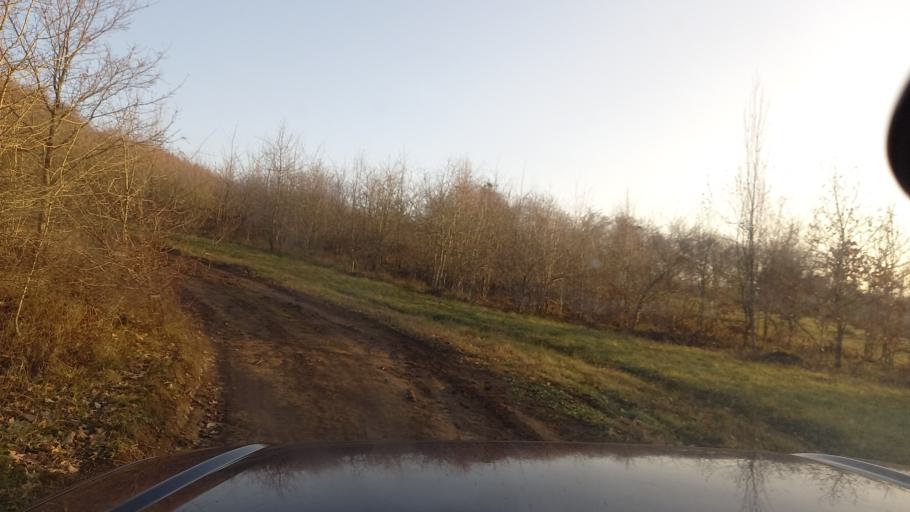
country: RU
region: Krasnodarskiy
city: Il'skiy
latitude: 44.8185
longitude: 38.5939
